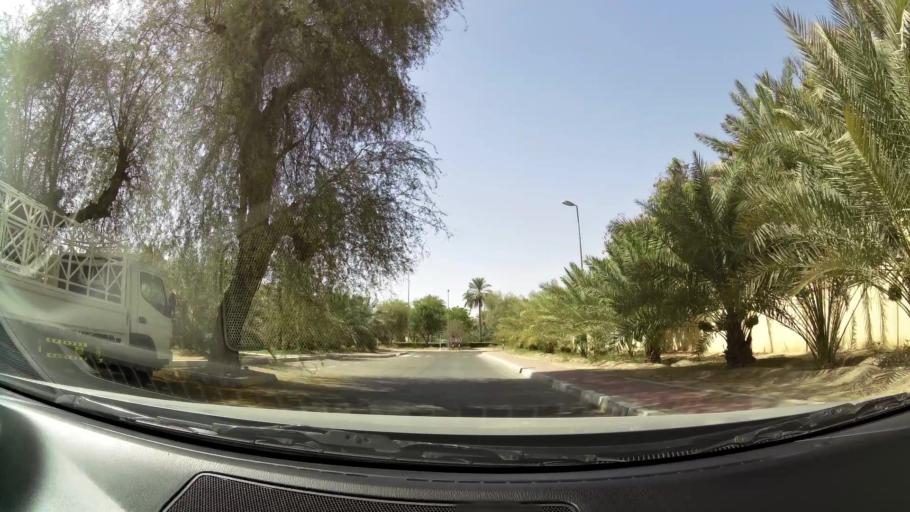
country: OM
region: Al Buraimi
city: Al Buraymi
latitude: 24.2976
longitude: 55.7753
